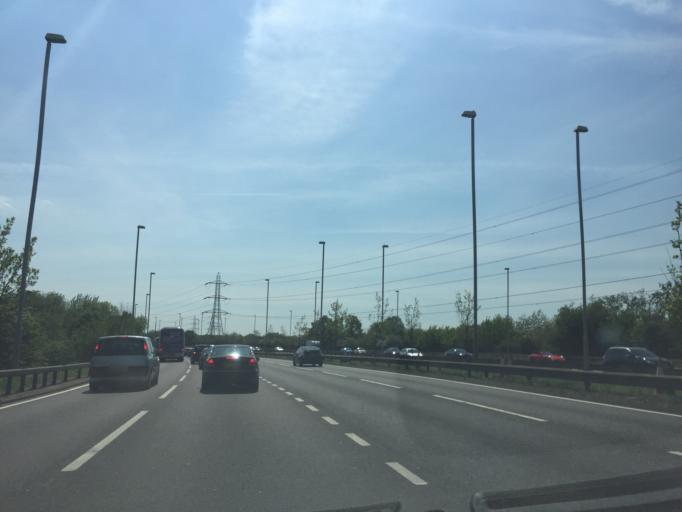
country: GB
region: England
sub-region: Greater London
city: Woodford Green
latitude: 51.5841
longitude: 0.0400
